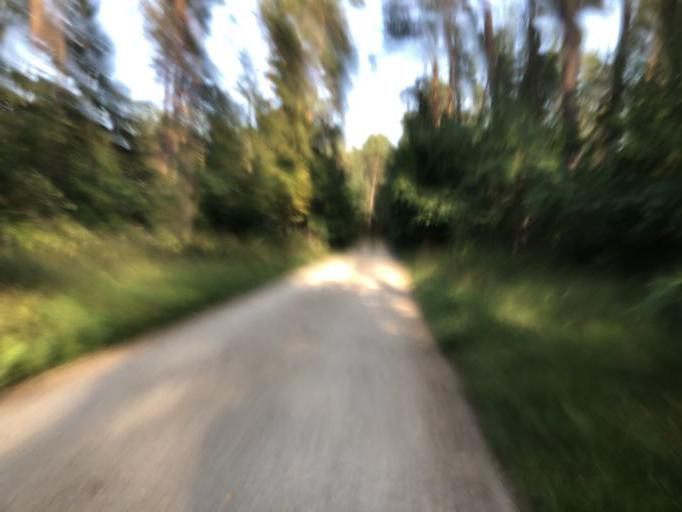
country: DE
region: Bavaria
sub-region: Regierungsbezirk Mittelfranken
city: Uttenreuth
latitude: 49.5678
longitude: 11.0878
